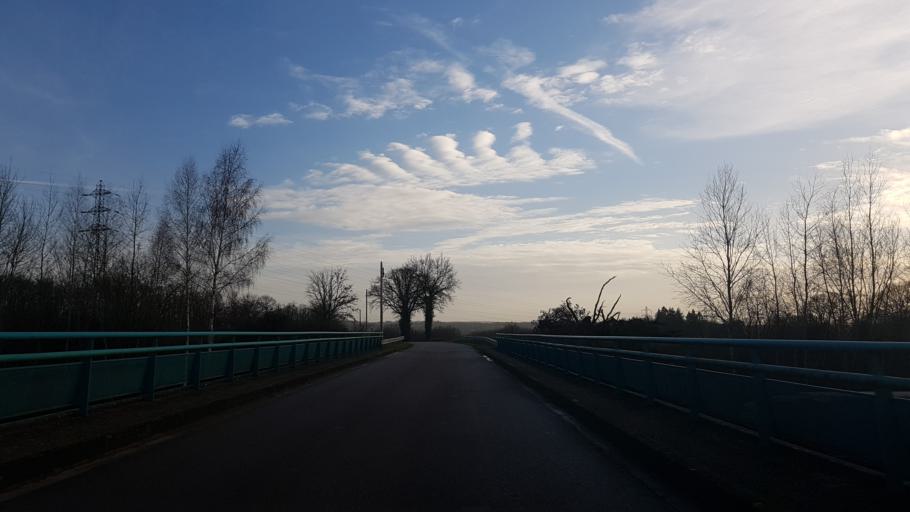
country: FR
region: Limousin
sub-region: Departement de la Haute-Vienne
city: Saint-Junien
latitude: 45.9039
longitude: 0.8548
